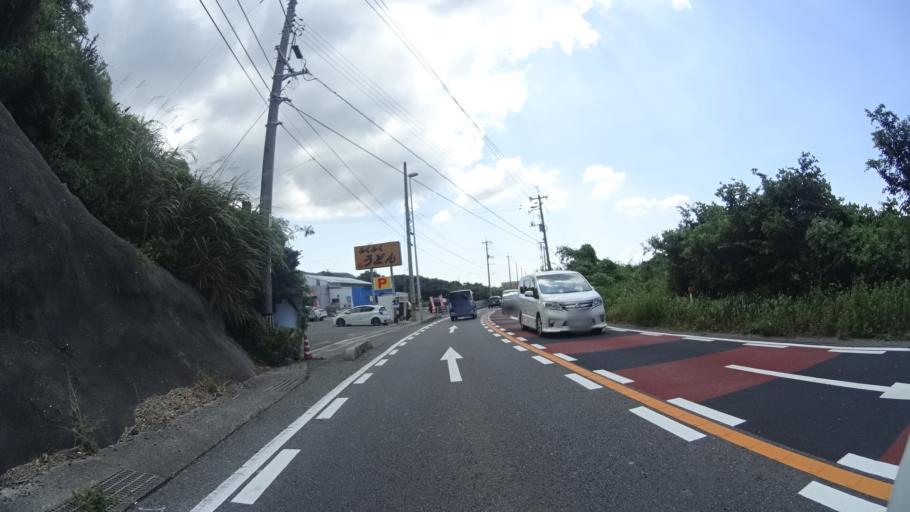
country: JP
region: Yamaguchi
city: Shimonoseki
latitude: 34.0538
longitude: 130.9129
